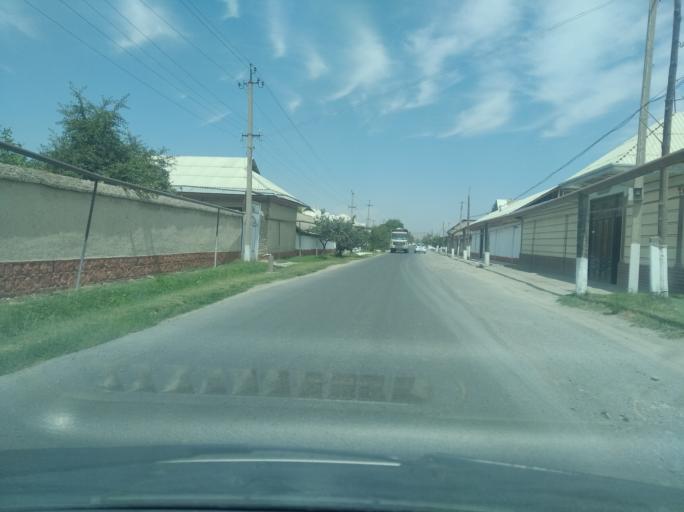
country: KG
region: Osh
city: Aravan
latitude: 40.6085
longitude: 72.4580
